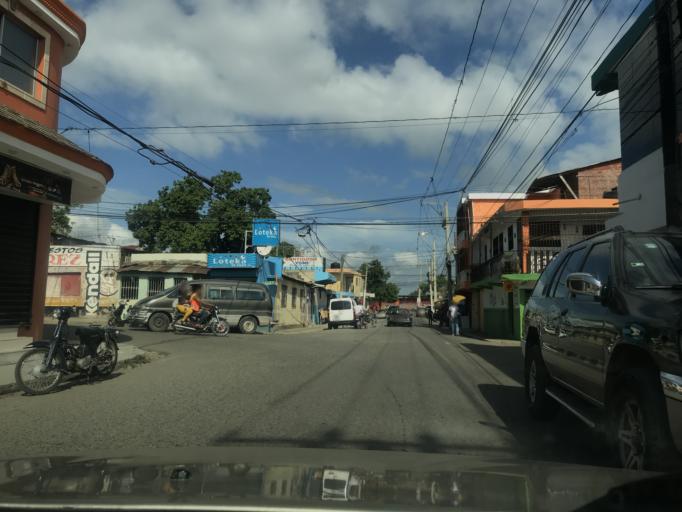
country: DO
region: Santiago
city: Palmar Arriba
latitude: 19.4853
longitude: -70.7465
